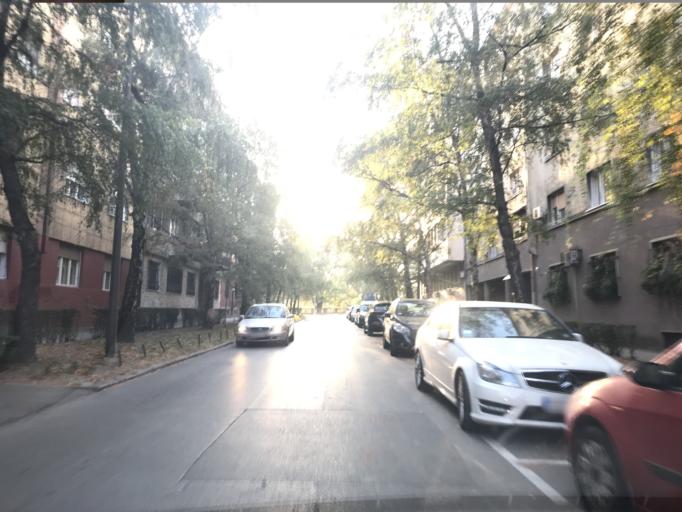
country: RS
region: Autonomna Pokrajina Vojvodina
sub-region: Juznobacki Okrug
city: Novi Sad
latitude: 45.2555
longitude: 19.8532
